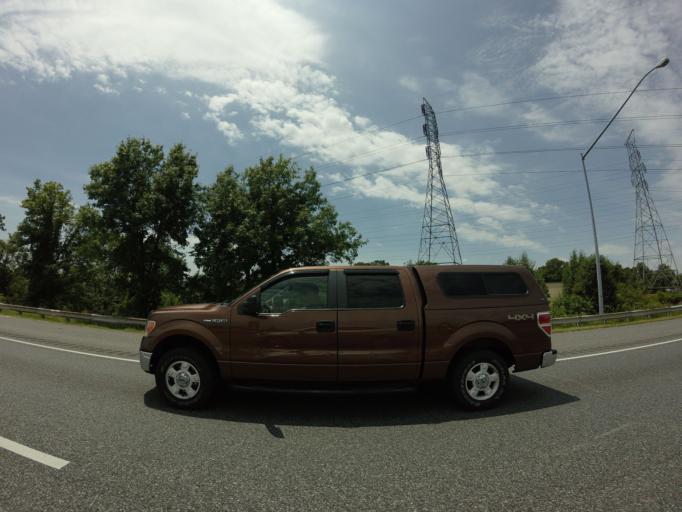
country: US
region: Maryland
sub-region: Baltimore County
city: Rosedale
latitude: 39.3086
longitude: -76.5017
